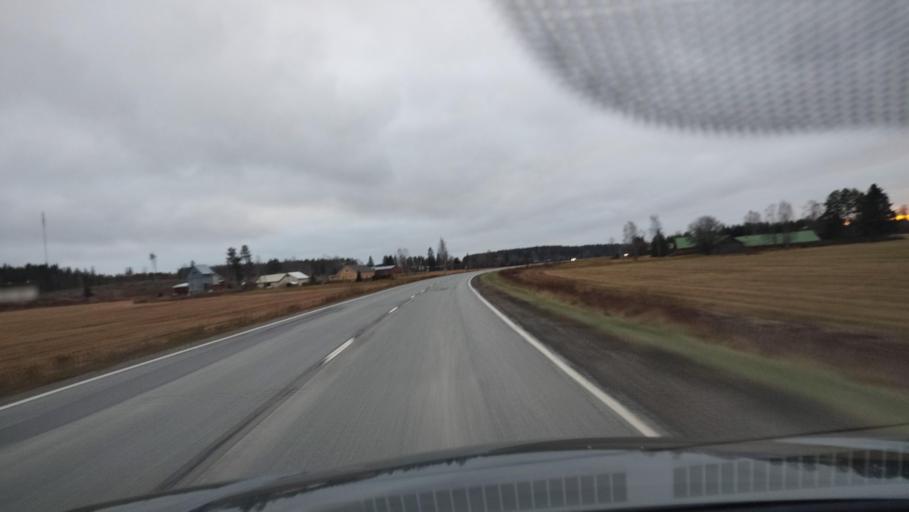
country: FI
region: Southern Ostrobothnia
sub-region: Suupohja
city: Kauhajoki
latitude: 62.3616
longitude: 22.0717
